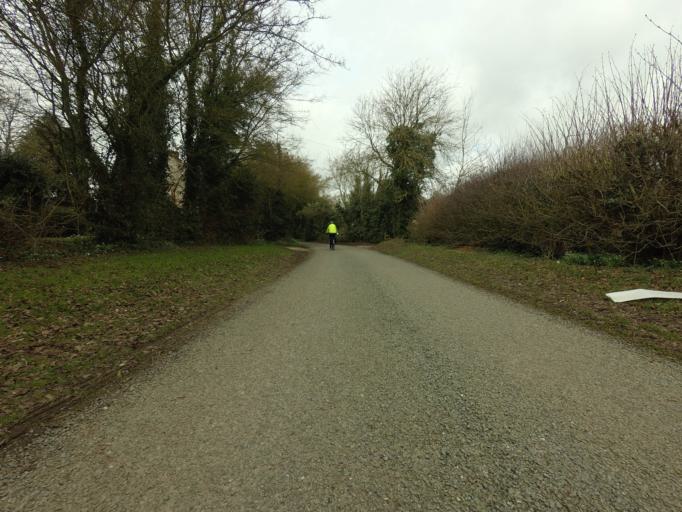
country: GB
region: England
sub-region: Lincolnshire
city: Grantham
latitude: 52.8723
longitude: -0.6613
